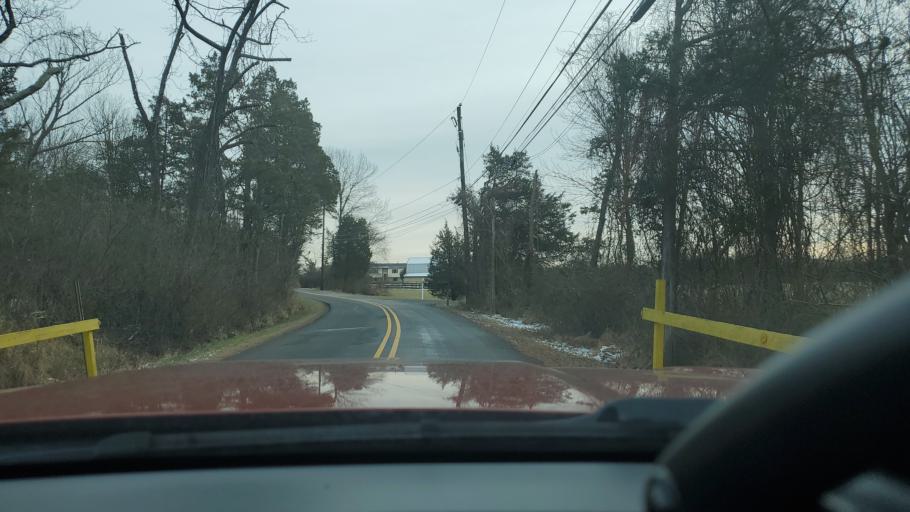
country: US
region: Pennsylvania
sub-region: Montgomery County
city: Woxall
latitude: 40.3177
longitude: -75.5107
